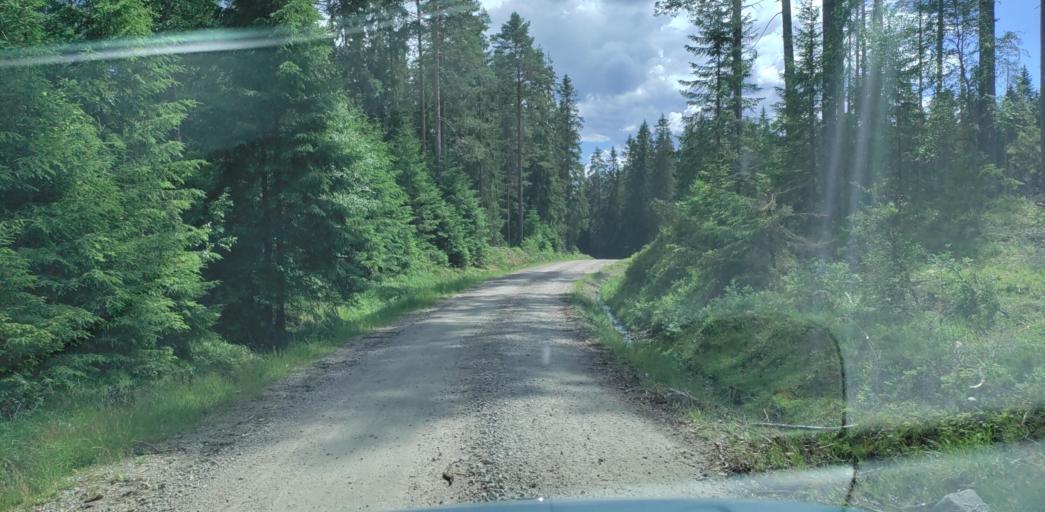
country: SE
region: Vaermland
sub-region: Hagfors Kommun
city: Ekshaerad
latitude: 60.0432
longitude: 13.3120
